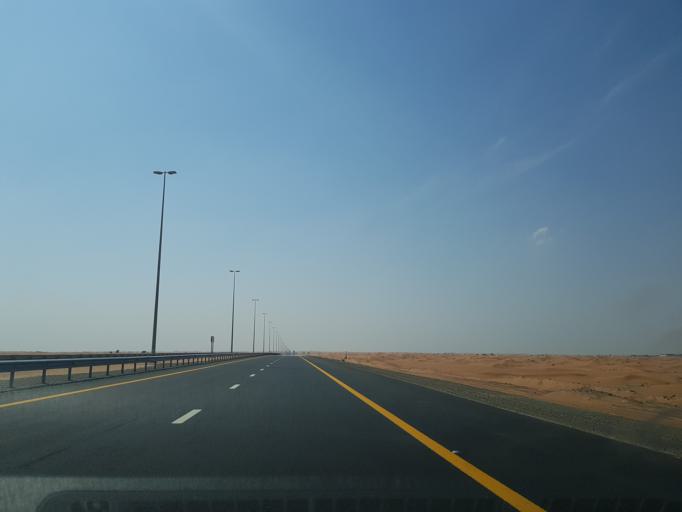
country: AE
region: Ash Shariqah
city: Adh Dhayd
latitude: 25.2536
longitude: 55.7603
